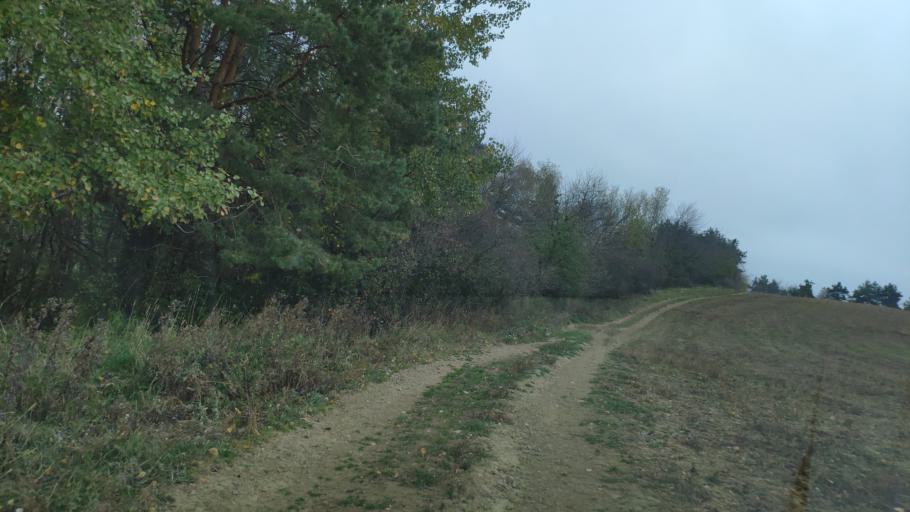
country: SK
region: Presovsky
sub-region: Okres Presov
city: Presov
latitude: 48.9291
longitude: 21.0954
